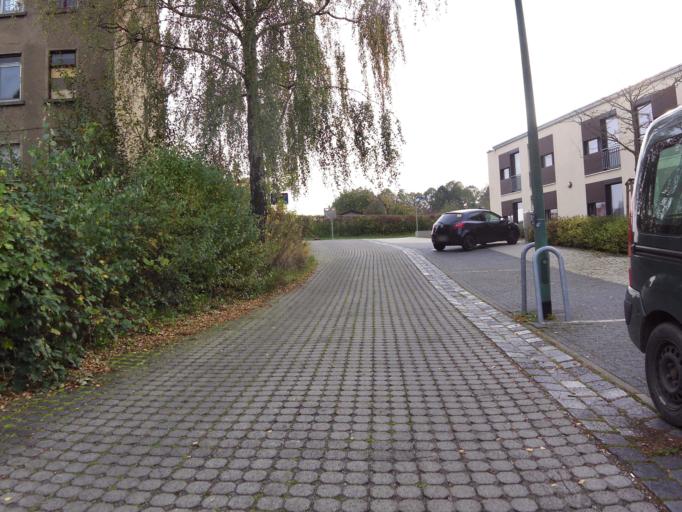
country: DE
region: Saxony
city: Taucha
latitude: 51.3805
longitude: 12.4398
